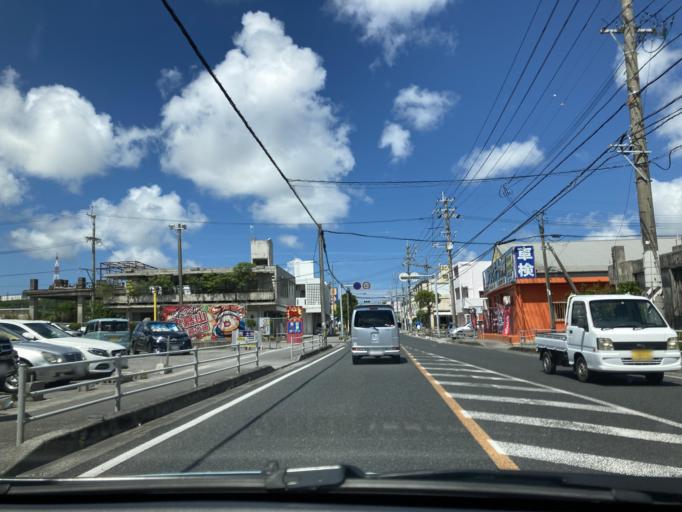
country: JP
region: Okinawa
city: Tomigusuku
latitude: 26.1813
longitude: 127.7155
